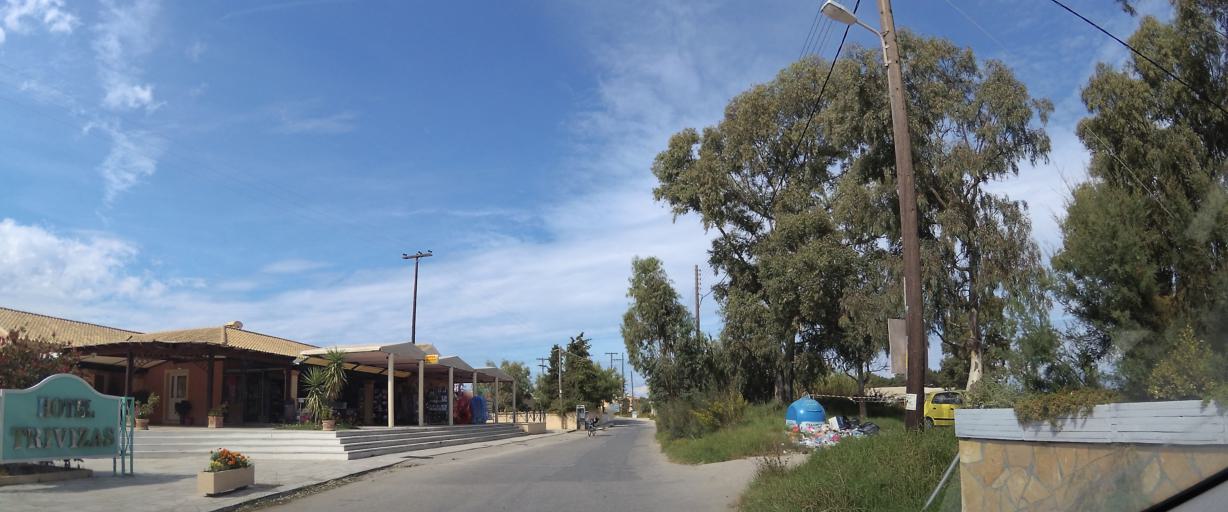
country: GR
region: Ionian Islands
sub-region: Nomos Kerkyras
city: Agios Georgis
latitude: 39.7932
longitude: 19.7023
